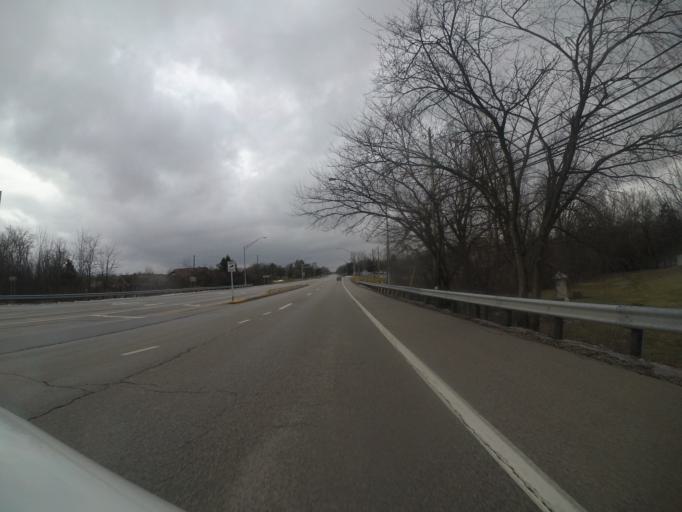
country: US
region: Ohio
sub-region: Wood County
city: Perrysburg
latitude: 41.5650
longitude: -83.5892
